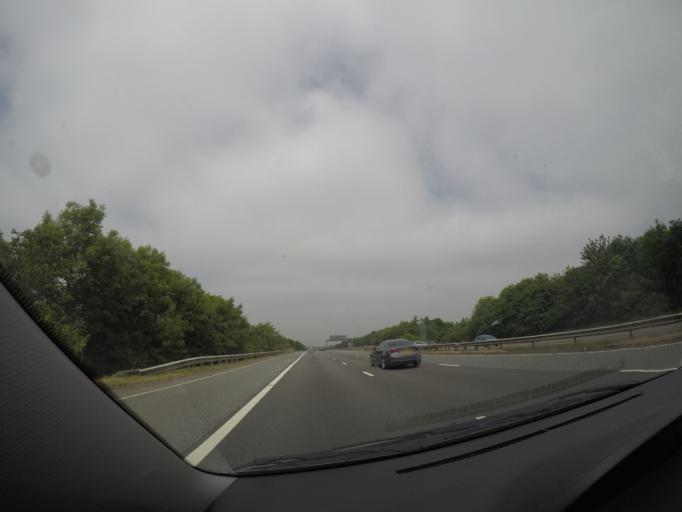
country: GB
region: England
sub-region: North Yorkshire
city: Boroughbridge
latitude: 54.0909
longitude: -1.4051
